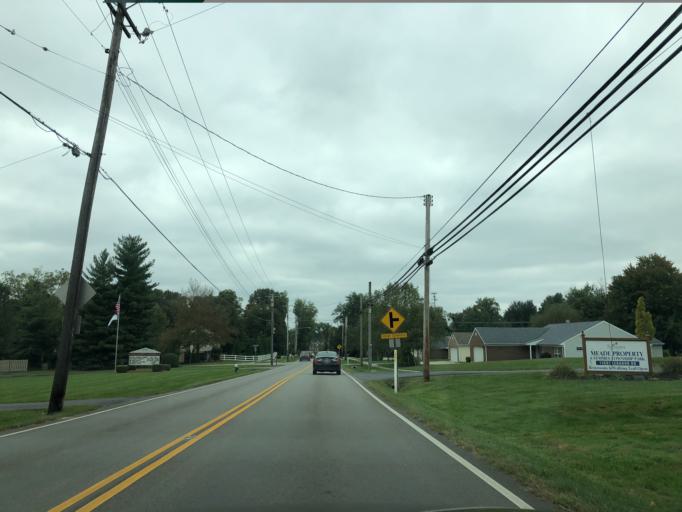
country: US
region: Ohio
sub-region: Hamilton County
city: Loveland
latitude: 39.2824
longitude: -84.2841
